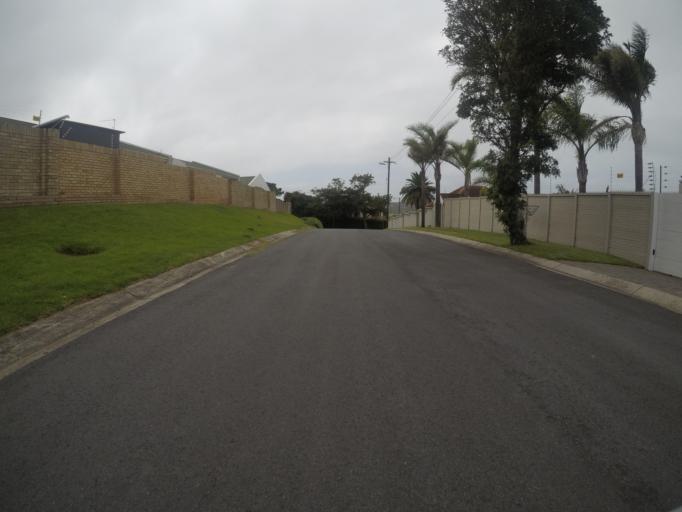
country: ZA
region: Eastern Cape
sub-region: Buffalo City Metropolitan Municipality
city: East London
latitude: -32.9897
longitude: 27.9350
